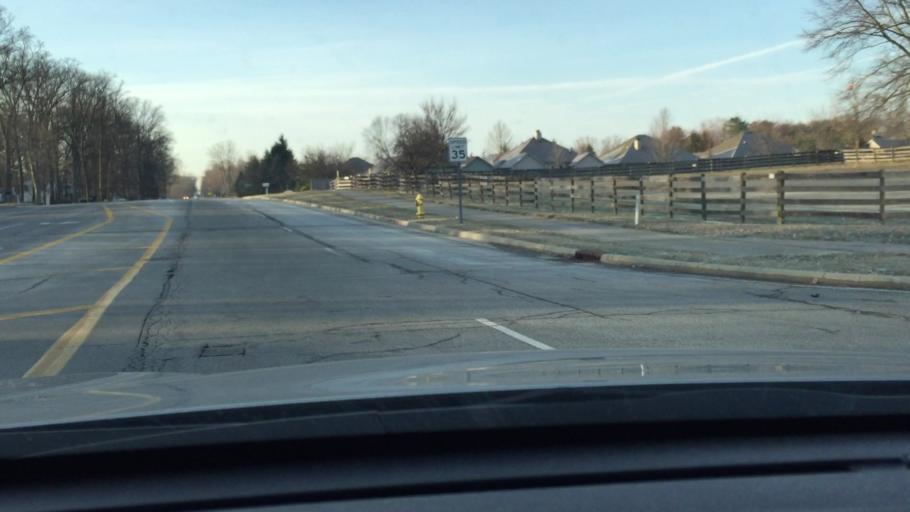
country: US
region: Indiana
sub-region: Hamilton County
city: Carmel
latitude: 39.9563
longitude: -86.1460
